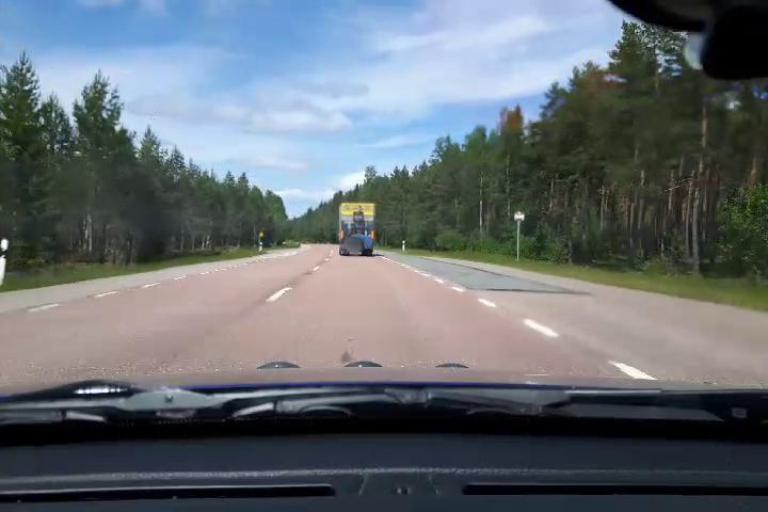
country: SE
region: Uppsala
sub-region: Osthammars Kommun
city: Bjorklinge
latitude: 60.1308
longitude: 17.5094
